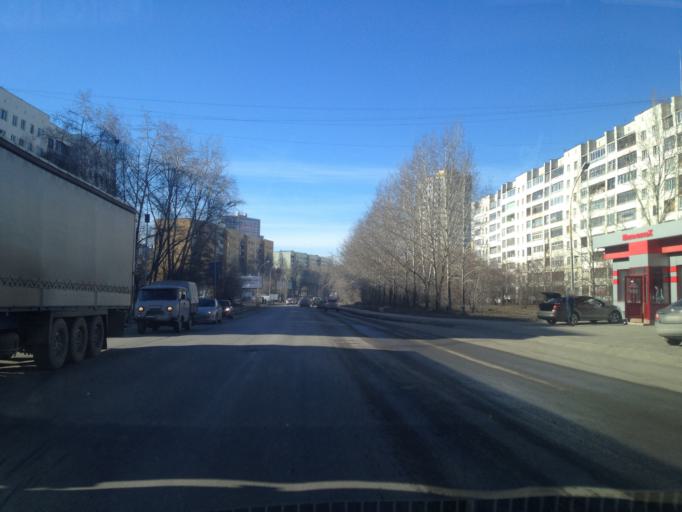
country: RU
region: Sverdlovsk
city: Yekaterinburg
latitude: 56.9029
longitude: 60.6243
